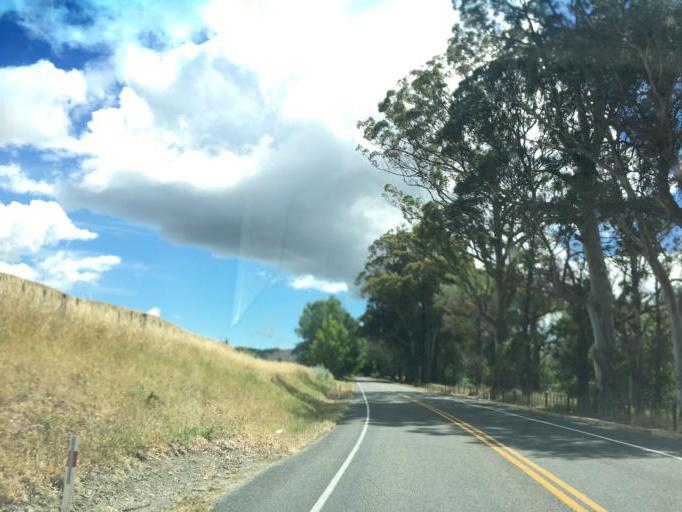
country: NZ
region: Hawke's Bay
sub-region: Hastings District
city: Hastings
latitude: -39.7127
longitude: 176.9287
